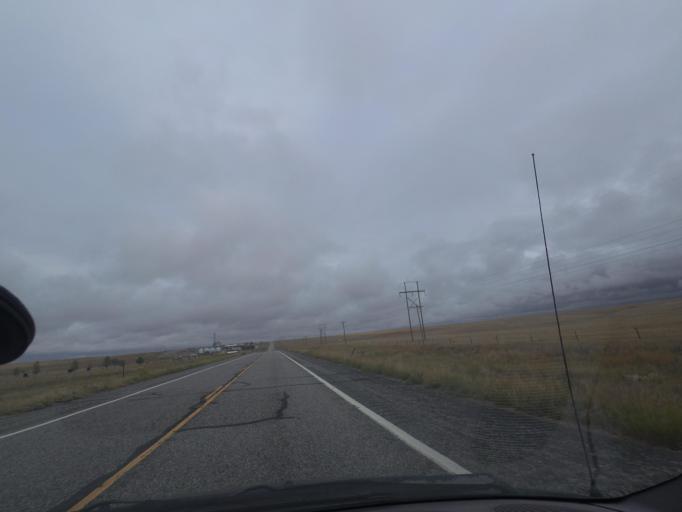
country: US
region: Colorado
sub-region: Washington County
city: Akron
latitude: 39.7393
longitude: -103.3559
